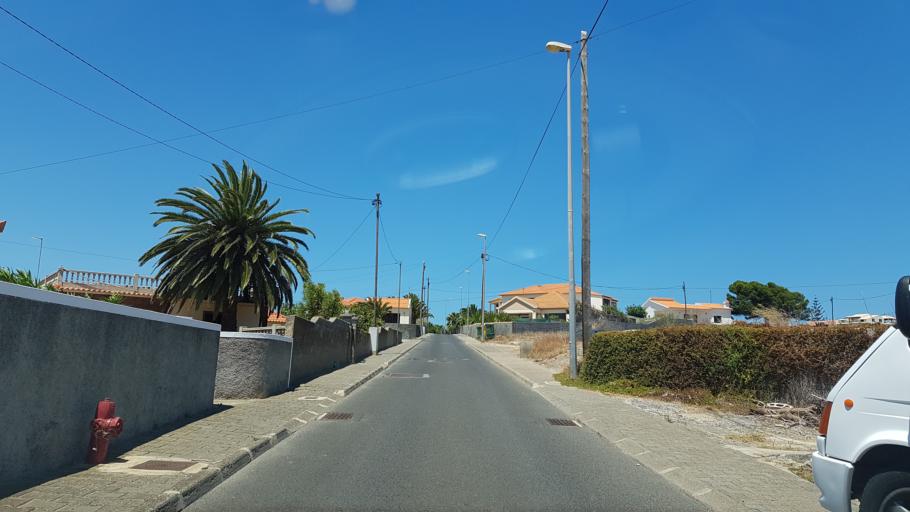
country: PT
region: Madeira
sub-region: Porto Santo
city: Vila de Porto Santo
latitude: 33.0536
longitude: -16.3599
